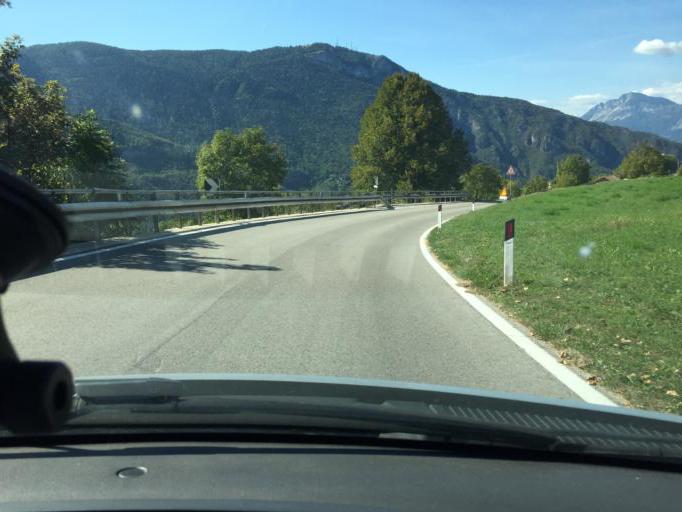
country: IT
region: Trentino-Alto Adige
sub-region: Provincia di Trento
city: Folgaria
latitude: 45.9126
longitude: 11.1599
